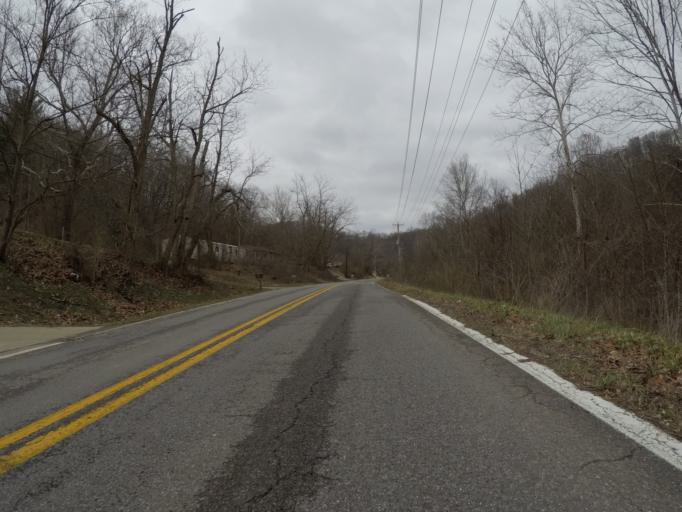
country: US
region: West Virginia
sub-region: Cabell County
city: Barboursville
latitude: 38.4571
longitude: -82.2992
